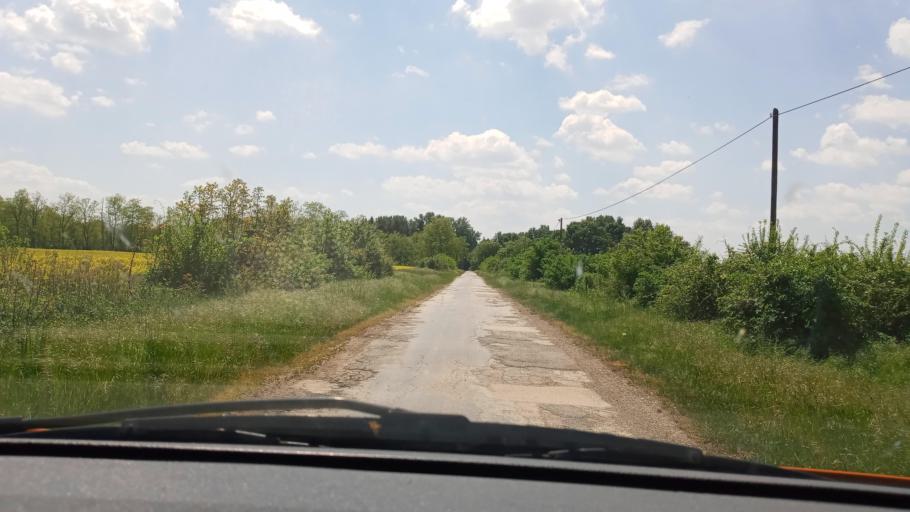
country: HU
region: Baranya
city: Siklos
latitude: 45.7753
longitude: 18.2755
